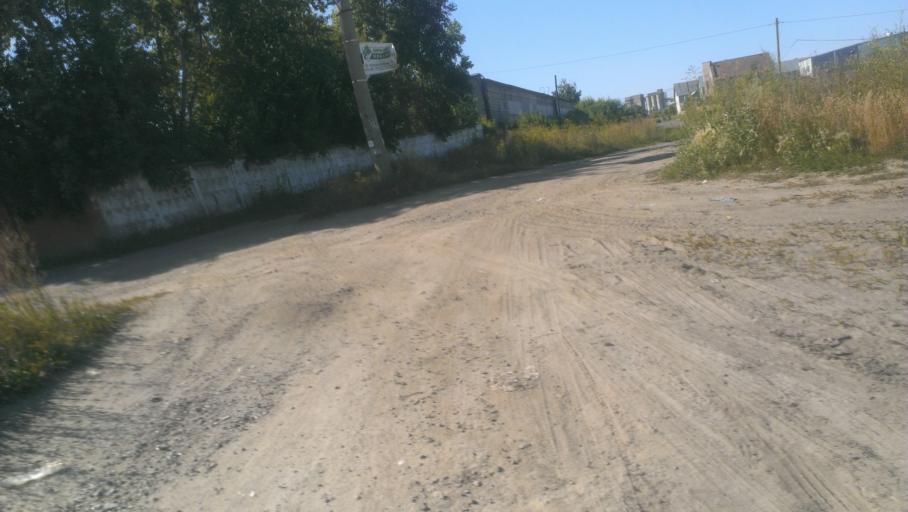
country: RU
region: Altai Krai
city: Novosilikatnyy
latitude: 53.3241
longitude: 83.6438
